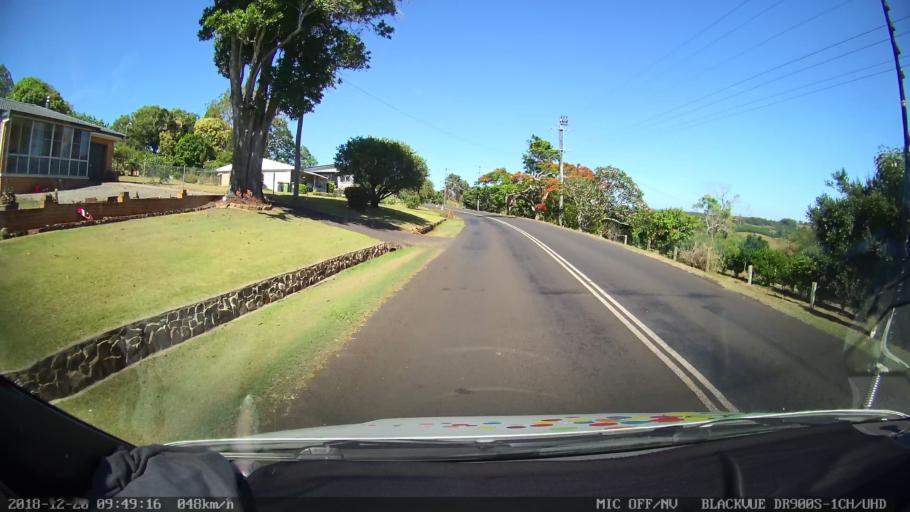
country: AU
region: New South Wales
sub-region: Lismore Municipality
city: Lismore
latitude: -28.7739
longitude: 153.2869
